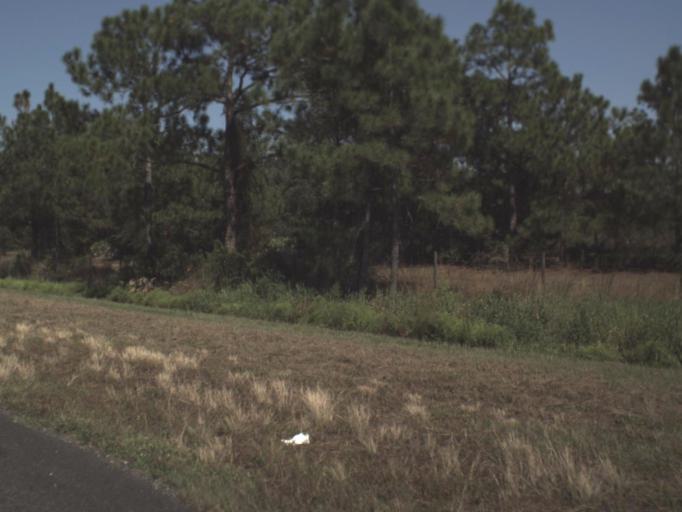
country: US
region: Florida
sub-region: Highlands County
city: Placid Lakes
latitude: 27.0721
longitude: -81.3360
